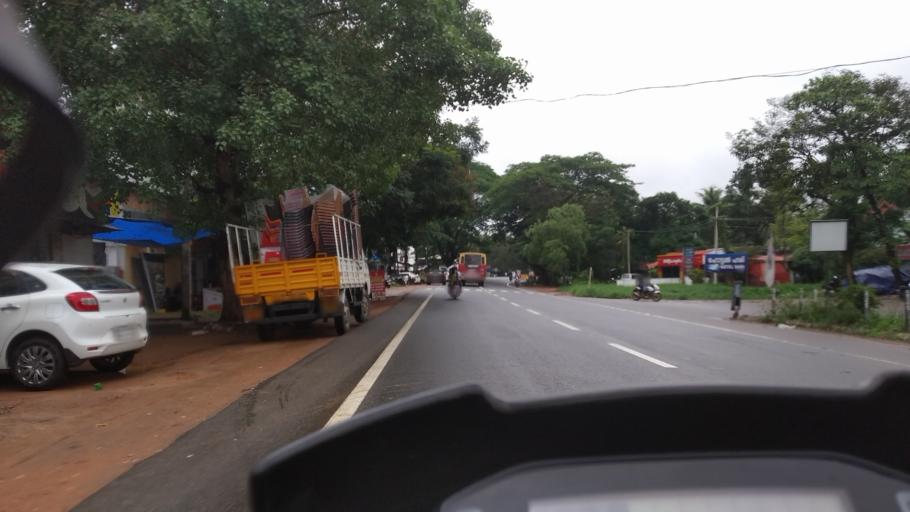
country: IN
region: Kerala
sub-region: Alappuzha
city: Mavelikara
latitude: 9.2837
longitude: 76.4409
